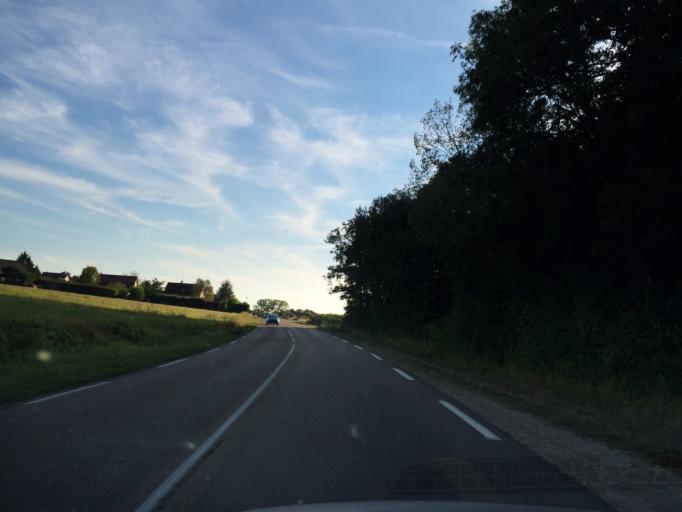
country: FR
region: Bourgogne
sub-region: Departement de l'Yonne
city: Saint-Georges-sur-Baulche
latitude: 47.8324
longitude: 3.5461
